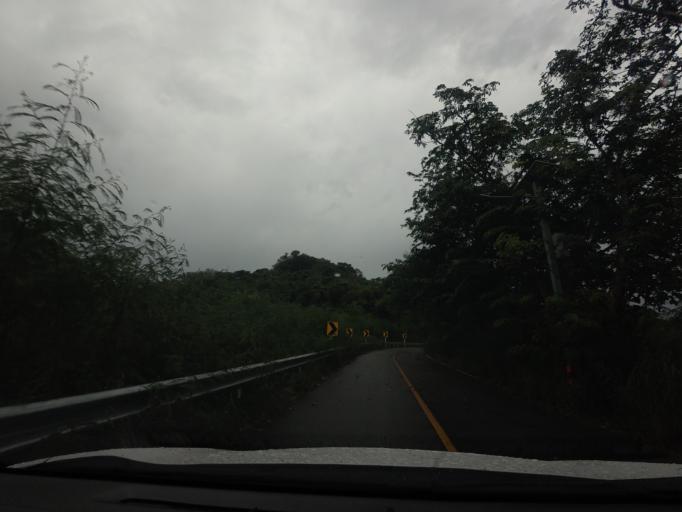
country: TH
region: Rayong
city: Ban Chang
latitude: 12.7676
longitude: 100.9523
